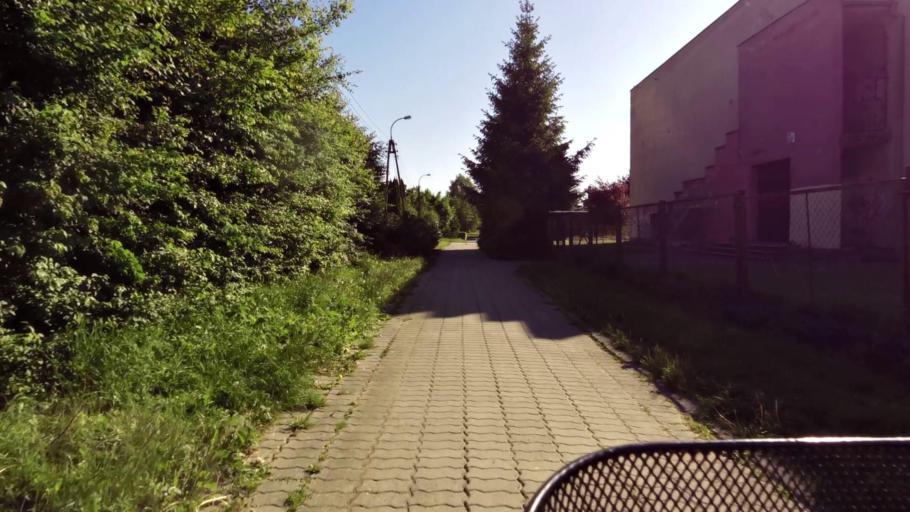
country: PL
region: West Pomeranian Voivodeship
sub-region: Koszalin
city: Koszalin
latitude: 54.1850
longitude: 16.2180
